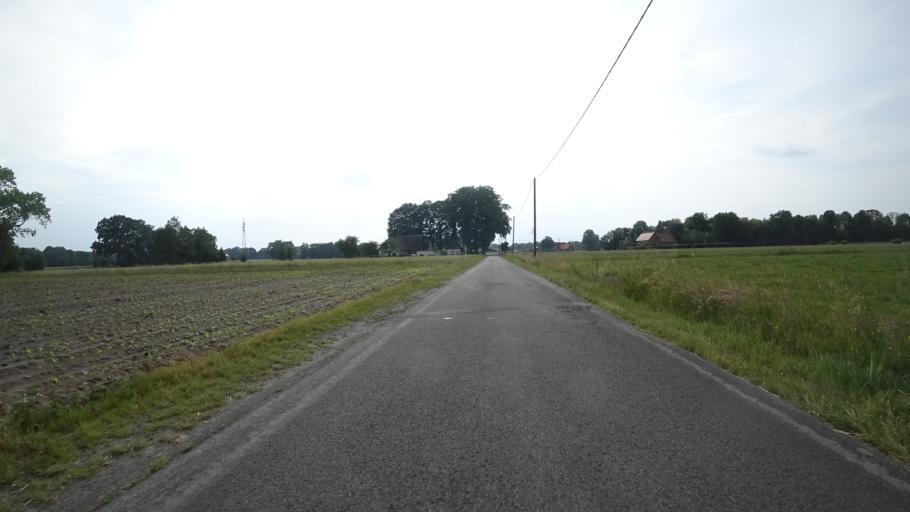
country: DE
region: North Rhine-Westphalia
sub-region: Regierungsbezirk Detmold
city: Guetersloh
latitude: 51.9474
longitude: 8.3583
